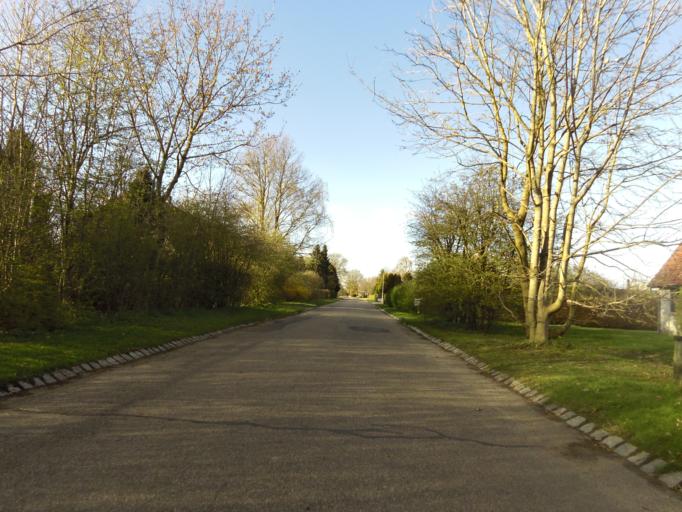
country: DK
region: South Denmark
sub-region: Tonder Kommune
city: Toftlund
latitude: 55.2320
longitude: 9.1237
